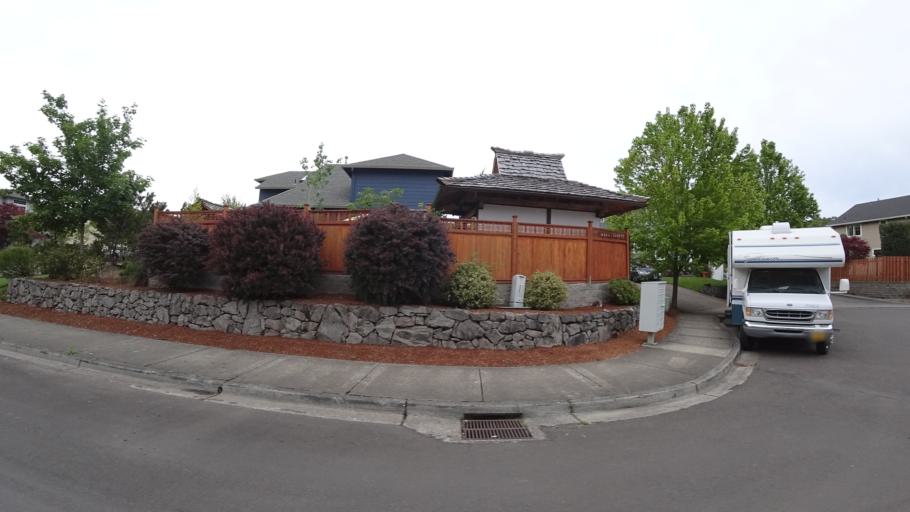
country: US
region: Oregon
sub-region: Washington County
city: Aloha
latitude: 45.5074
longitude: -122.9083
